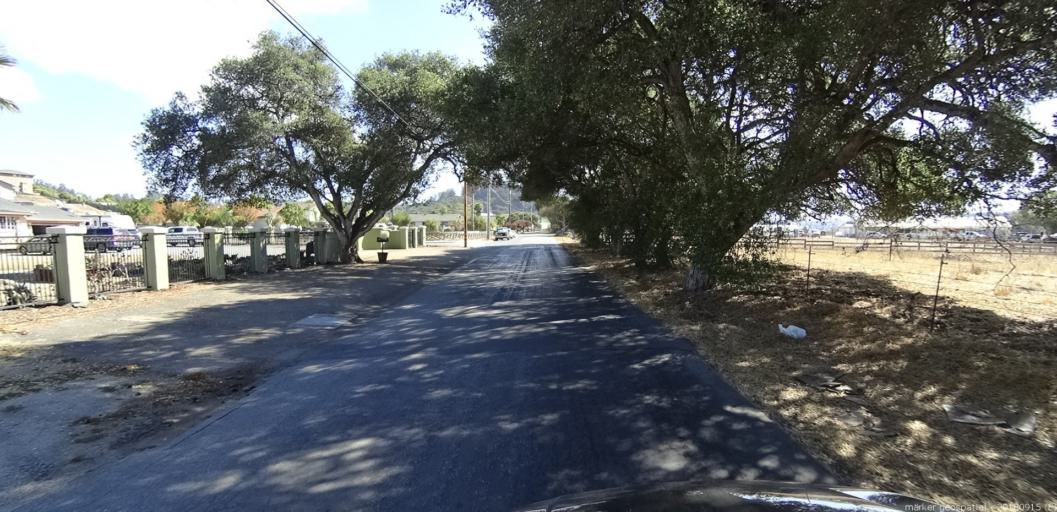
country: US
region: California
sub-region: Monterey County
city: Las Lomas
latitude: 36.8667
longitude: -121.7296
